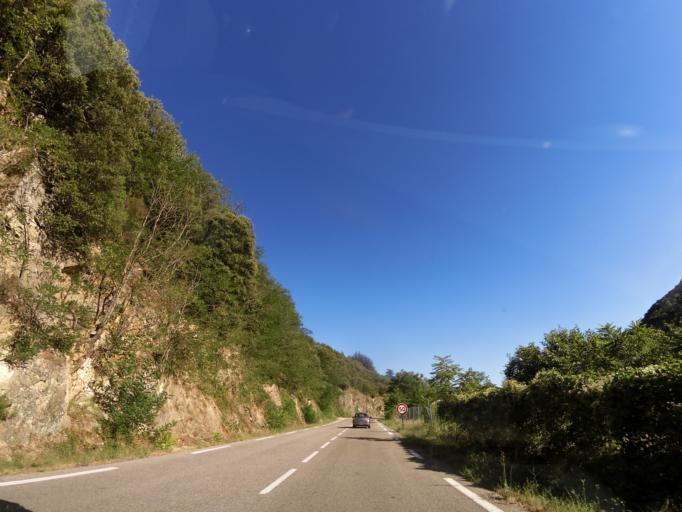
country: FR
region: Languedoc-Roussillon
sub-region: Departement du Gard
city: Valleraugue
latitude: 44.0628
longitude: 3.6834
